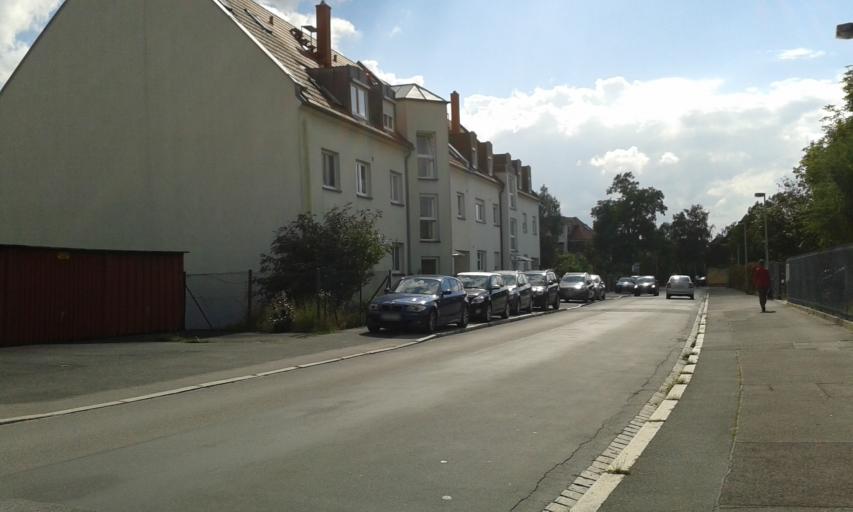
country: DE
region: Bavaria
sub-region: Upper Franconia
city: Bamberg
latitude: 49.8908
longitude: 10.9155
